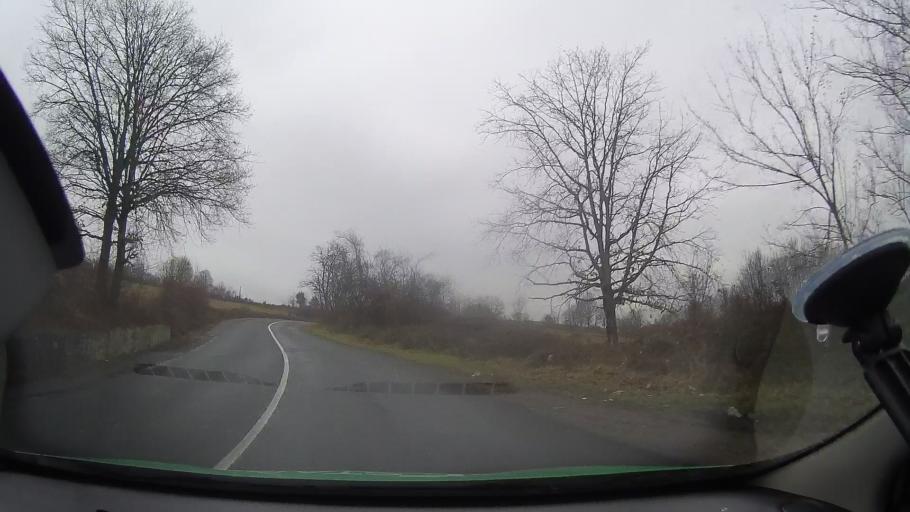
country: RO
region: Arad
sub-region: Comuna Varfurile
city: Varfurile
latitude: 46.3250
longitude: 22.4944
